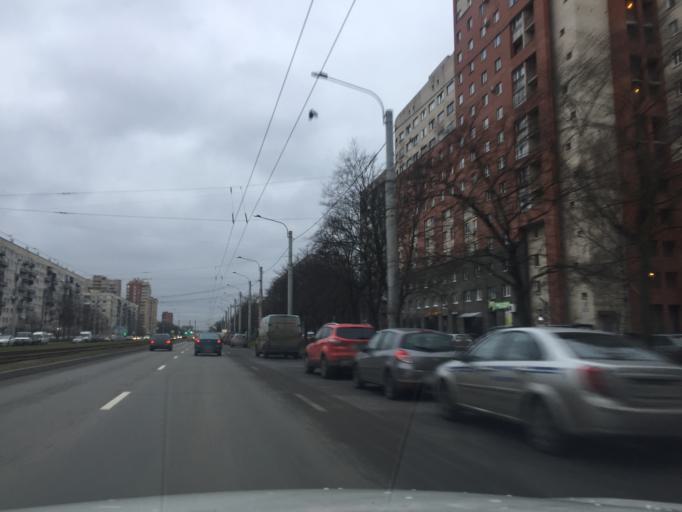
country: RU
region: St.-Petersburg
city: Grazhdanka
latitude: 60.0425
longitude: 30.4009
